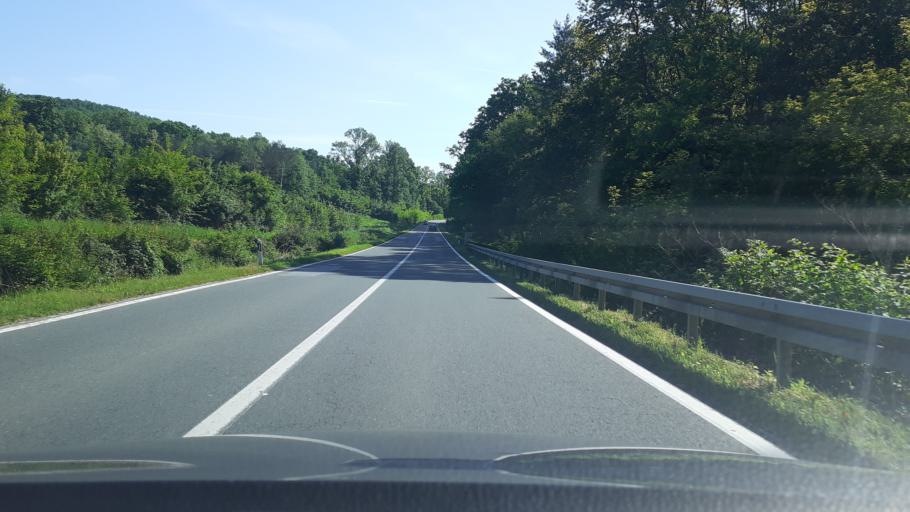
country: HR
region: Brodsko-Posavska
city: Batrina
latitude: 45.2072
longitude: 17.6811
